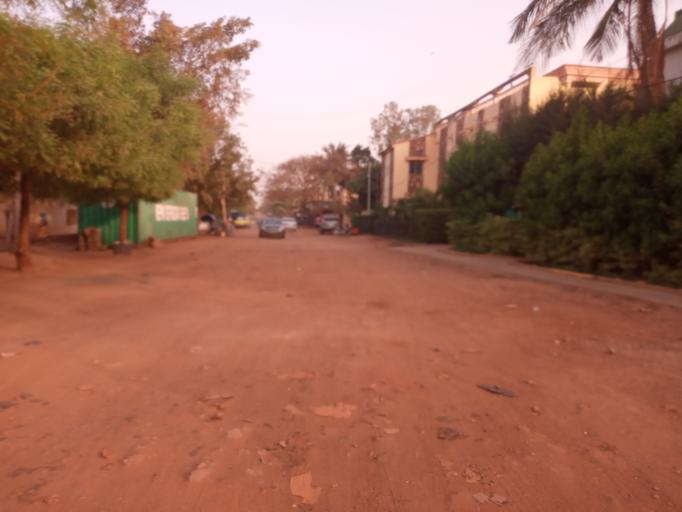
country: ML
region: Bamako
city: Bamako
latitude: 12.5862
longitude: -7.9528
